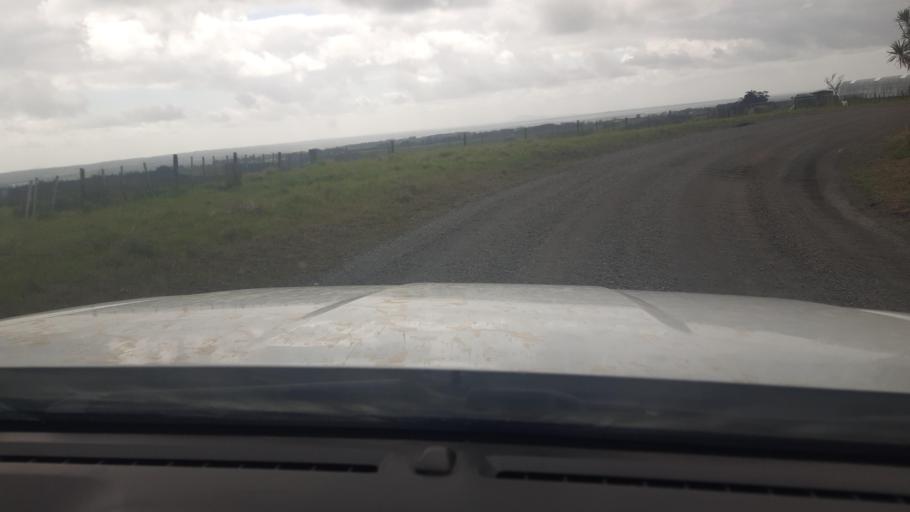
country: NZ
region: Northland
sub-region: Far North District
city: Kaitaia
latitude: -35.0624
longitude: 173.3224
